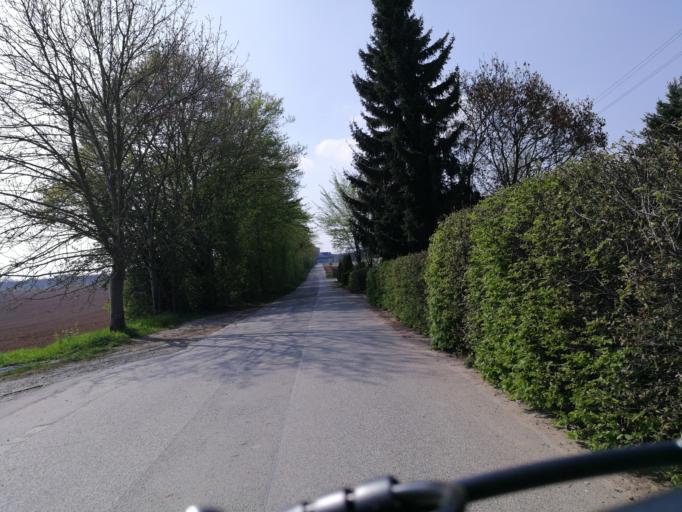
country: DE
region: North Rhine-Westphalia
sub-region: Regierungsbezirk Dusseldorf
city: Dormagen
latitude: 51.1179
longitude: 6.8064
